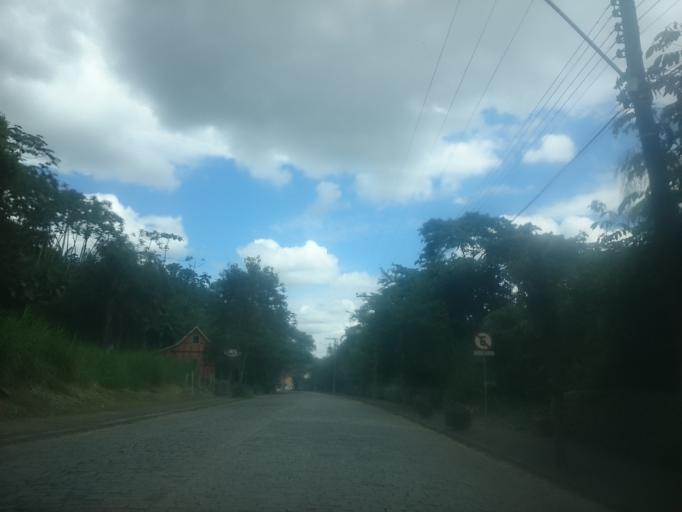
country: BR
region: Santa Catarina
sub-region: Pomerode
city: Pomerode
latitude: -26.7286
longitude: -49.1711
